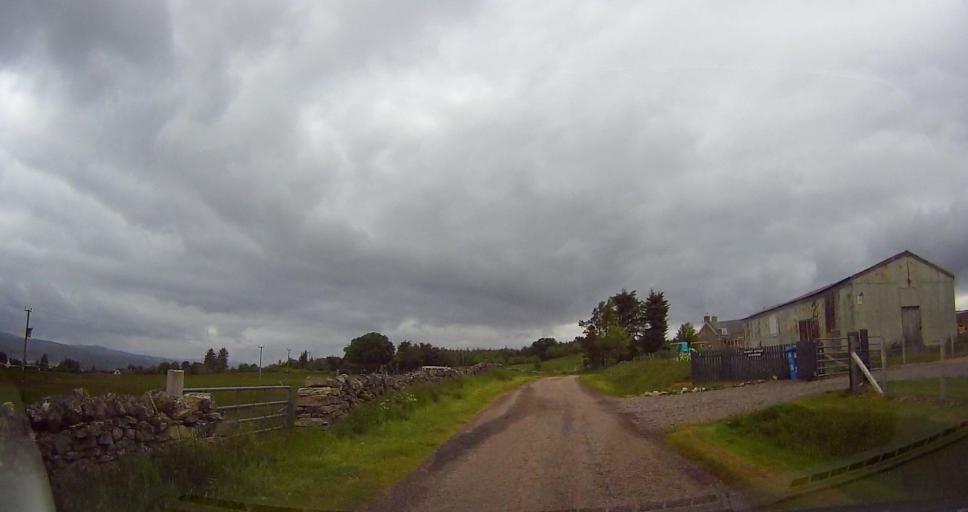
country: GB
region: Scotland
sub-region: Highland
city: Alness
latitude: 58.0791
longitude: -4.4462
